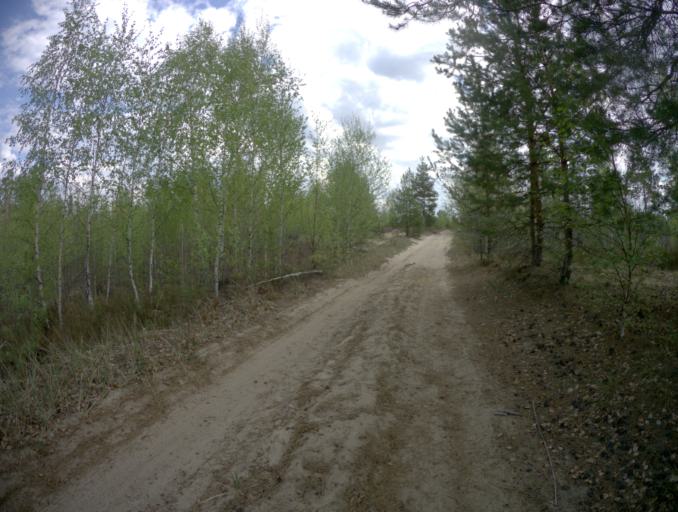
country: RU
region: Ivanovo
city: Talitsy
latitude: 56.4688
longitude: 42.2007
